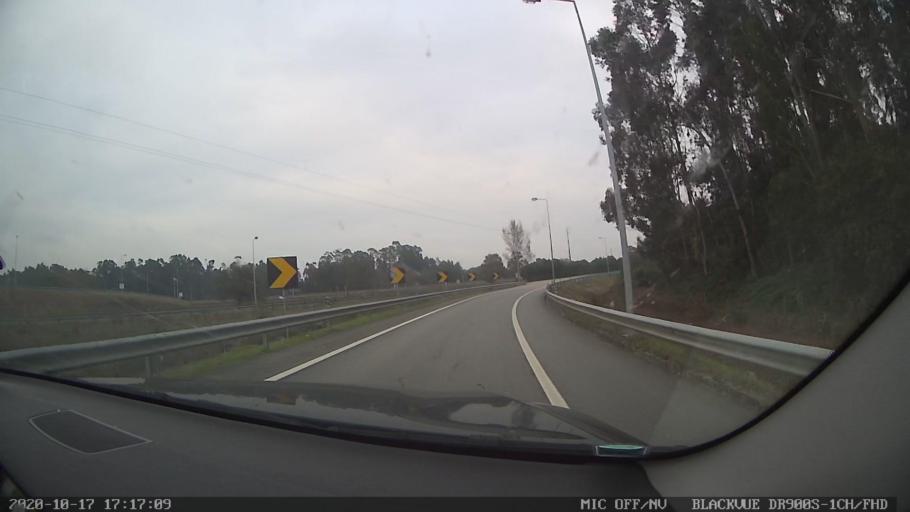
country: PT
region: Braga
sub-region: Esposende
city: Apulia
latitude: 41.4852
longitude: -8.7468
